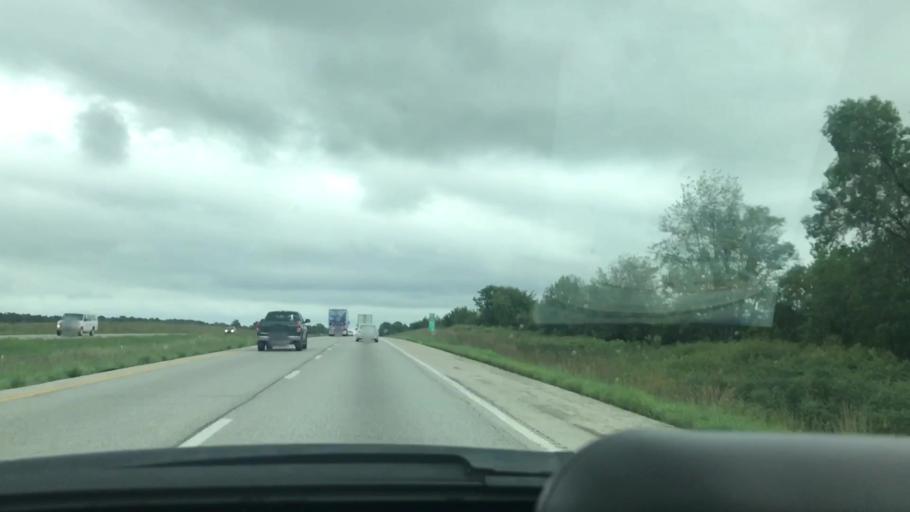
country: US
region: Missouri
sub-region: Greene County
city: Ash Grove
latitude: 37.1864
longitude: -93.6162
